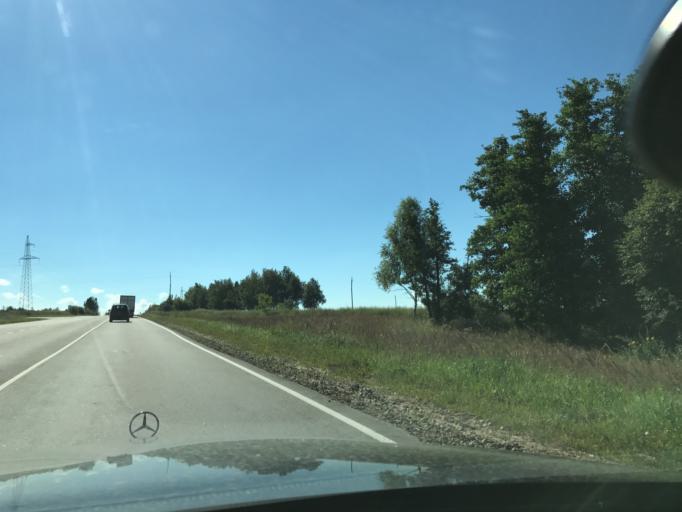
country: RU
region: Vladimir
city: Belaya Rechka
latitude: 56.2726
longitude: 39.4406
